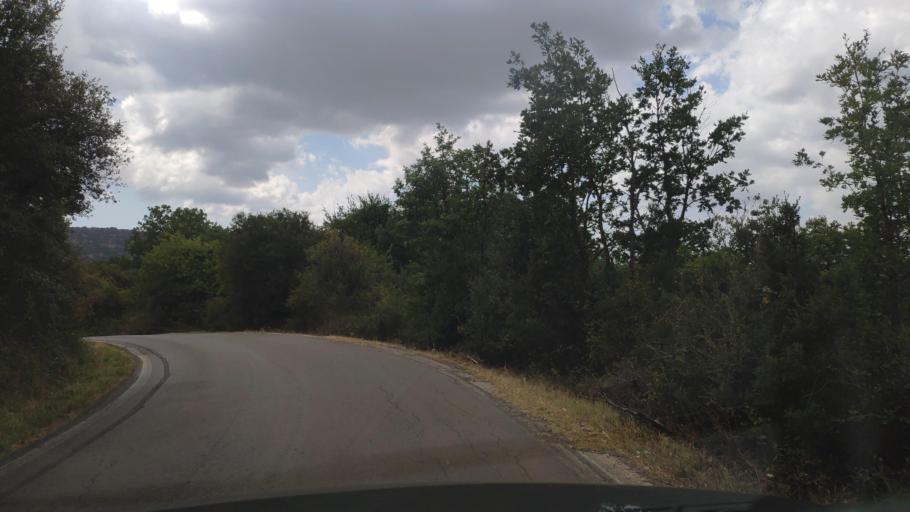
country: GR
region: Peloponnese
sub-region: Nomos Lakonias
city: Kariai
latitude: 37.3215
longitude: 22.4350
